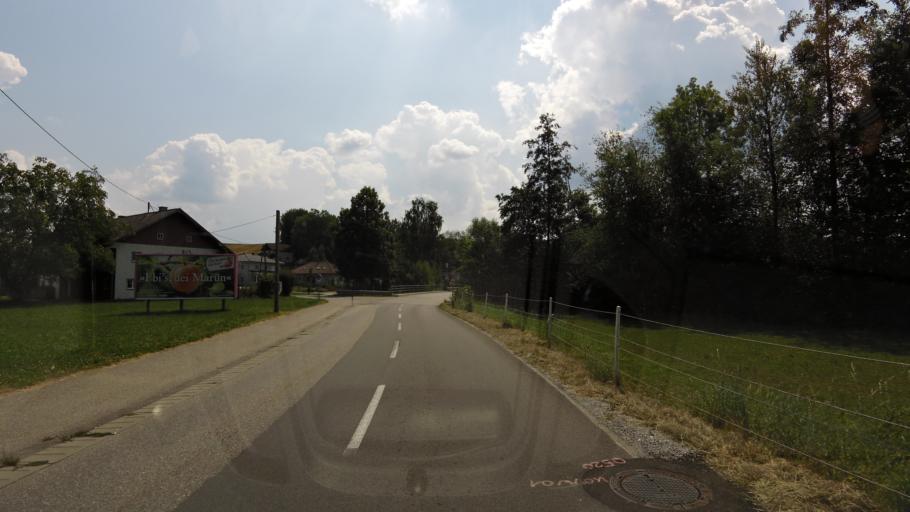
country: AT
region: Upper Austria
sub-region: Politischer Bezirk Ried im Innkreis
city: Waldzell
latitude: 48.1402
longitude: 13.4248
